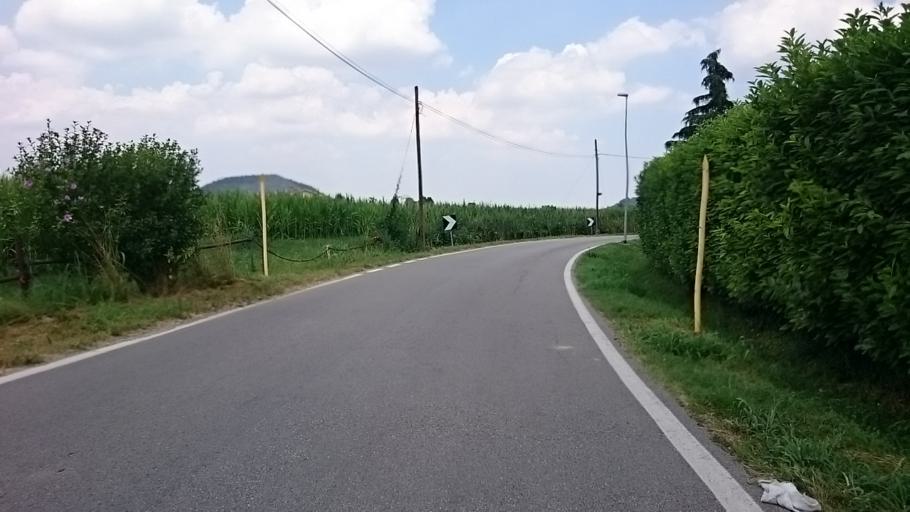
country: IT
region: Veneto
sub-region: Provincia di Padova
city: Torreglia
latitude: 45.3318
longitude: 11.7397
